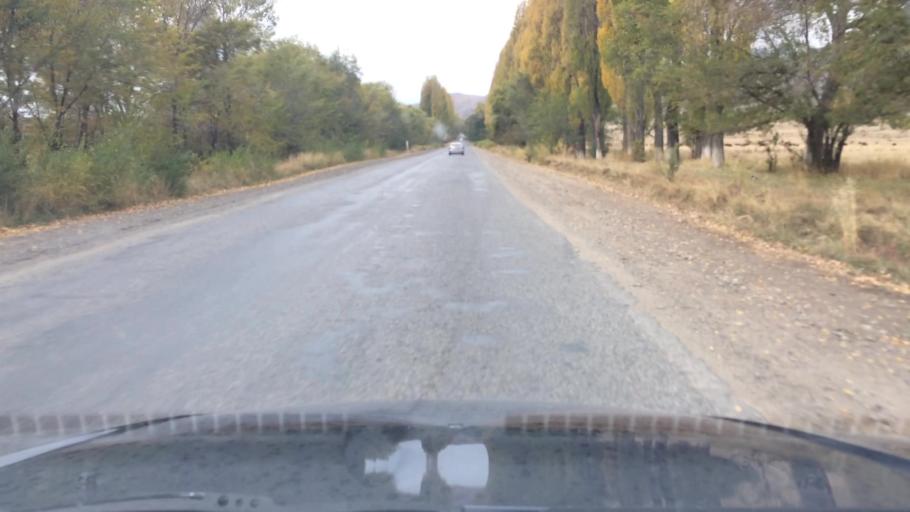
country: KG
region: Ysyk-Koel
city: Pokrovka
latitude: 42.7380
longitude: 77.9226
